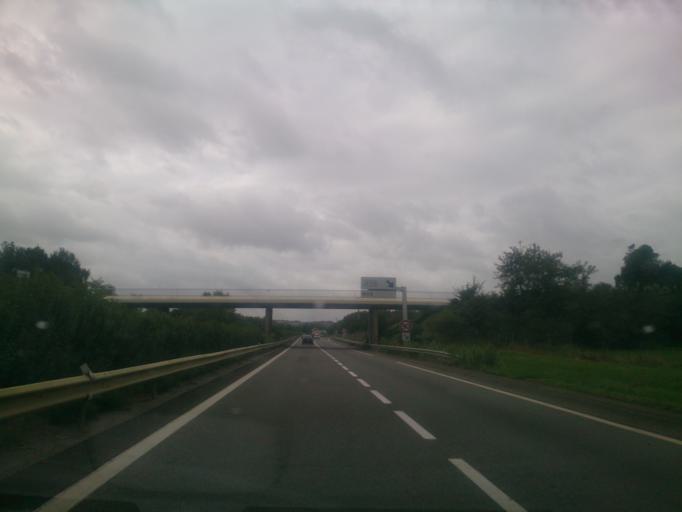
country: FR
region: Midi-Pyrenees
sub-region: Departement de la Haute-Garonne
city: Noe
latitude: 43.3568
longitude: 1.2694
